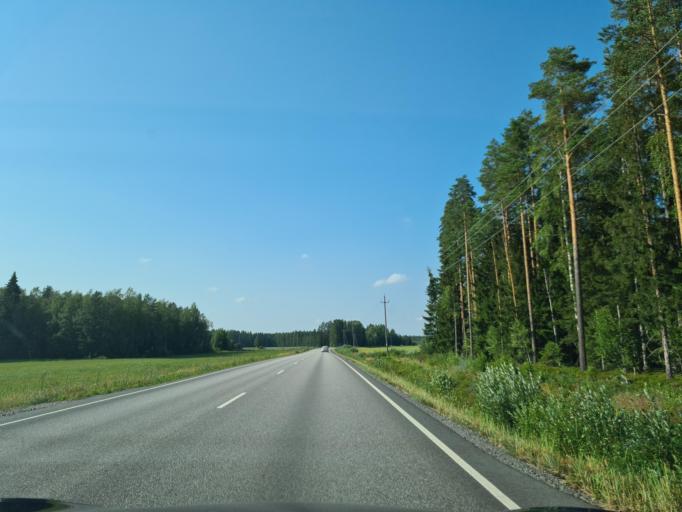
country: FI
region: Satakunta
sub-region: Pohjois-Satakunta
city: Karvia
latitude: 61.9611
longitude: 22.5112
